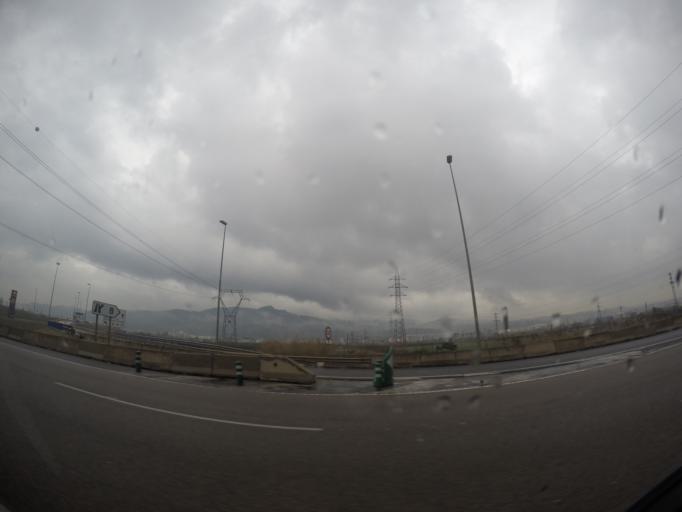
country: ES
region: Catalonia
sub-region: Provincia de Barcelona
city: Sant Vicenc dels Horts
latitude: 41.3901
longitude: 2.0259
